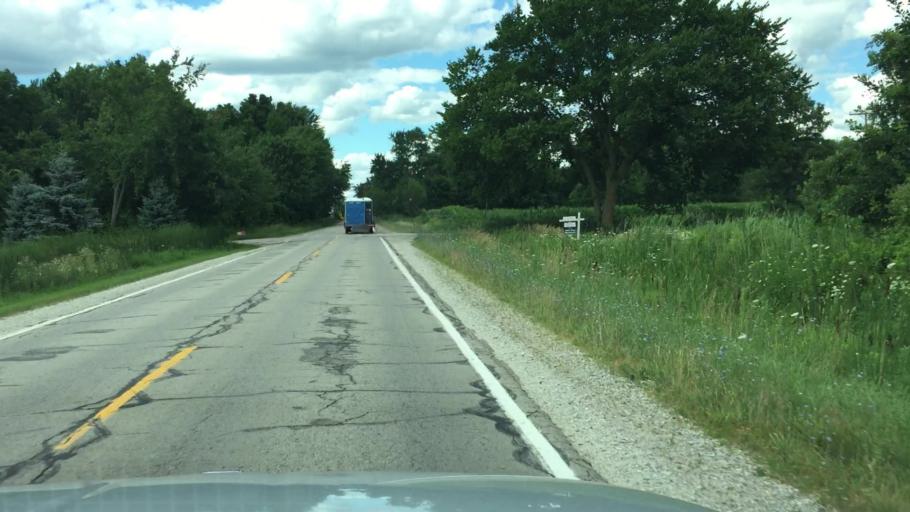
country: US
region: Michigan
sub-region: Saint Clair County
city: Capac
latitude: 42.9376
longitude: -82.9459
